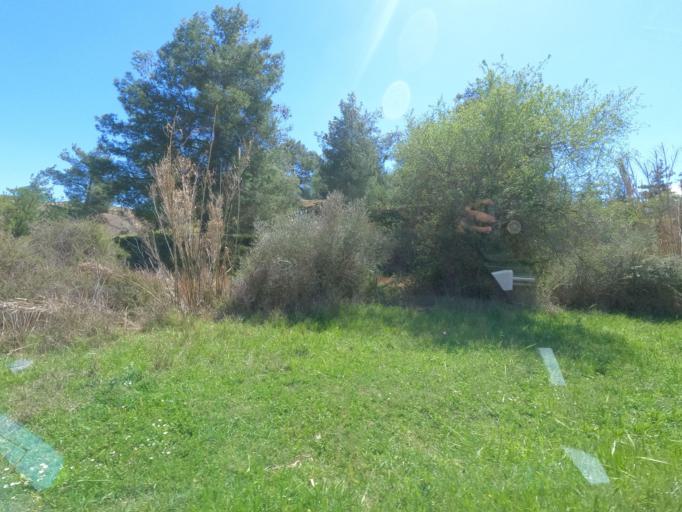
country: CY
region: Lefkosia
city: Peristerona
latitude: 35.0553
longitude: 33.0741
